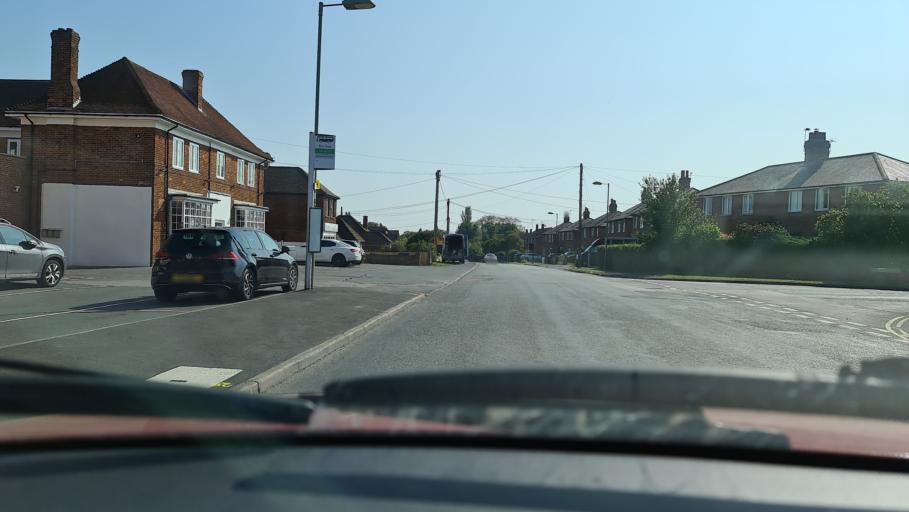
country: GB
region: England
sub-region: Oxfordshire
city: Bicester
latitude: 51.9048
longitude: -1.1605
